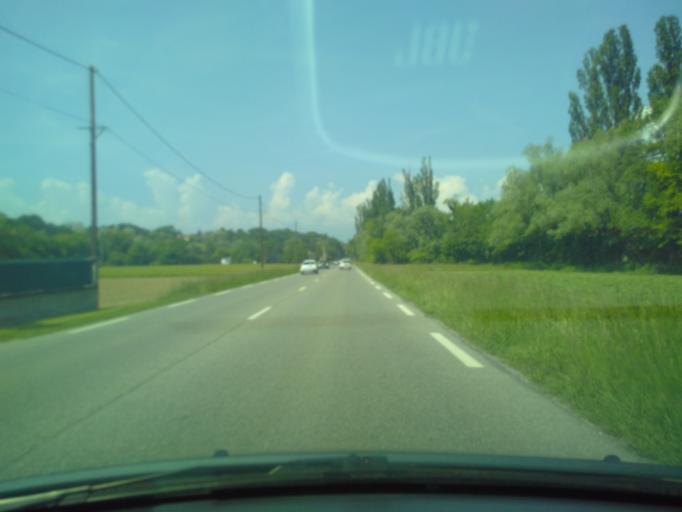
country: FR
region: Rhone-Alpes
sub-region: Departement de la Haute-Savoie
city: Archamps
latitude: 46.1425
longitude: 6.1149
